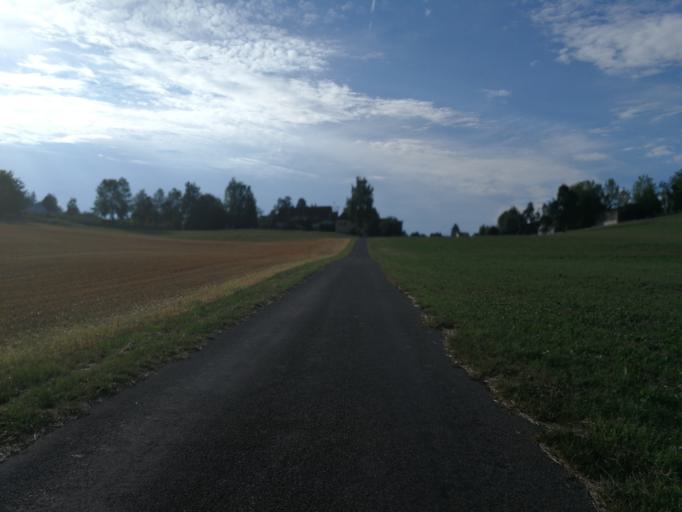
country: CH
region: Zurich
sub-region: Bezirk Meilen
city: Oetwil am See
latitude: 47.2703
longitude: 8.7364
